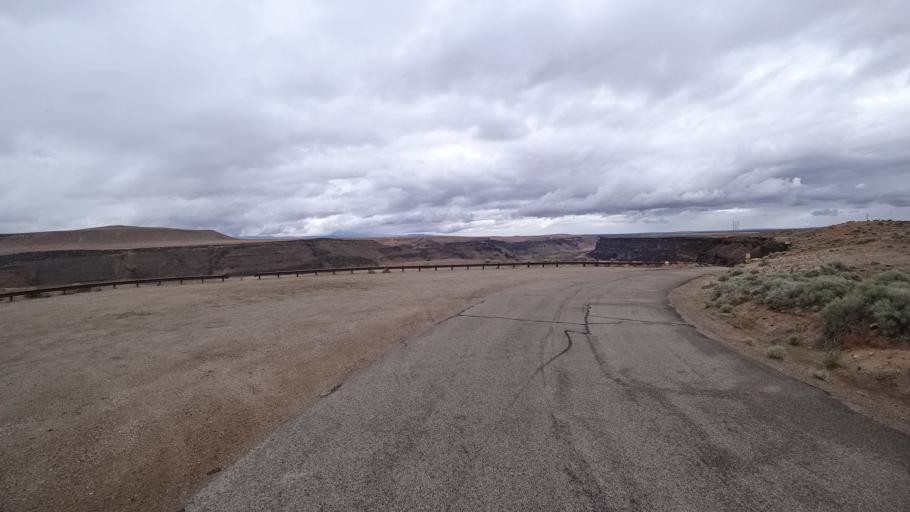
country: US
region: Idaho
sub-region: Owyhee County
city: Murphy
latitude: 43.2380
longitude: -116.3680
